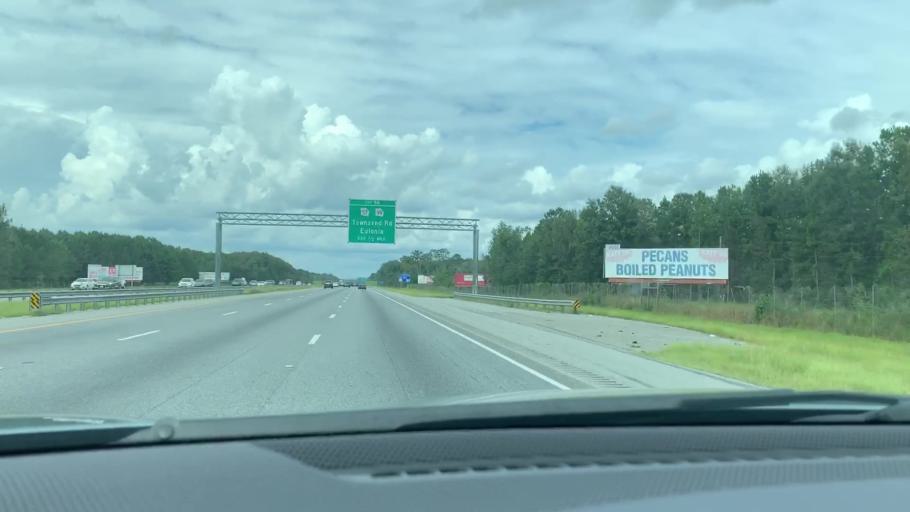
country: US
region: Georgia
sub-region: McIntosh County
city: Darien
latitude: 31.5196
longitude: -81.4454
